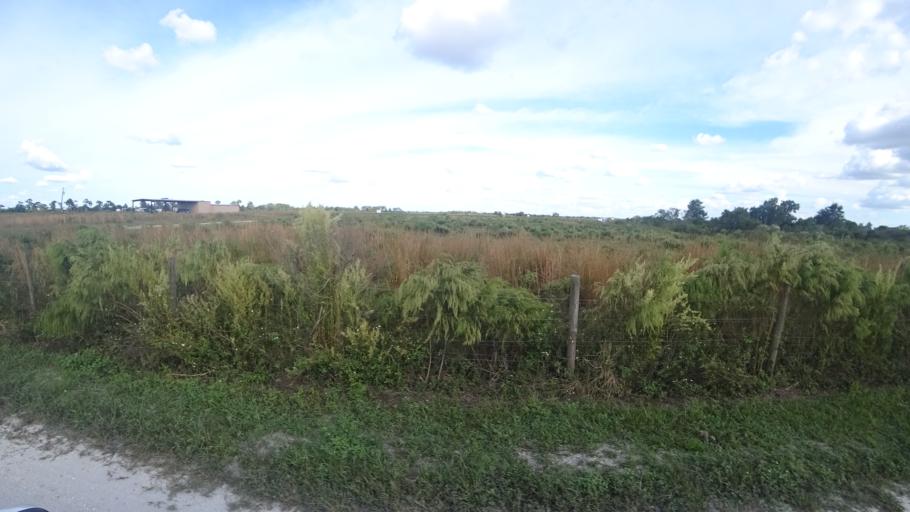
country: US
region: Florida
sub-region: DeSoto County
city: Arcadia
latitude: 27.2953
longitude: -82.1053
